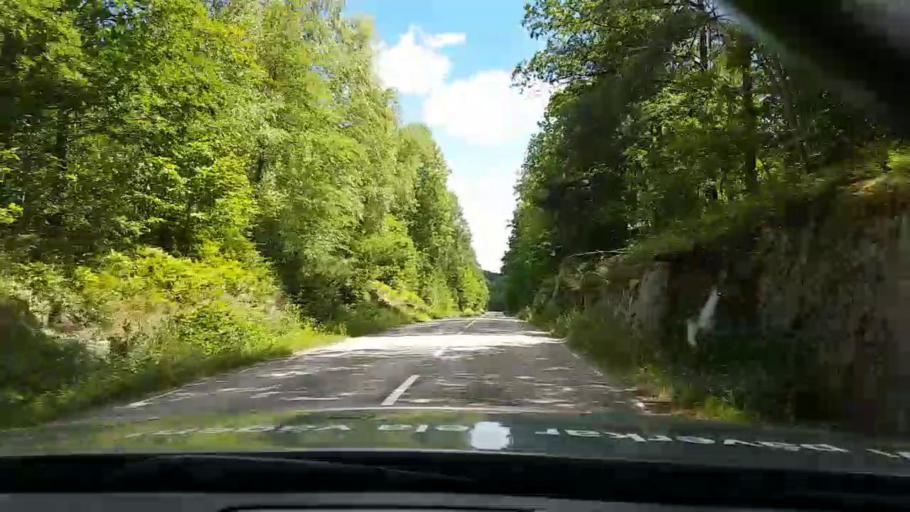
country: SE
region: Kalmar
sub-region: Vasterviks Kommun
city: Overum
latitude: 58.0702
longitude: 16.3842
